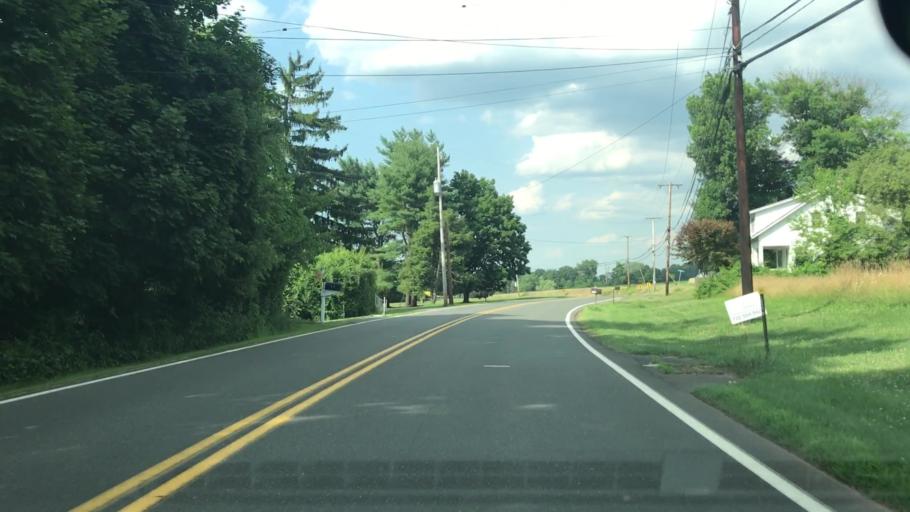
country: US
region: New Jersey
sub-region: Hunterdon County
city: Flemington
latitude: 40.4593
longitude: -74.8313
